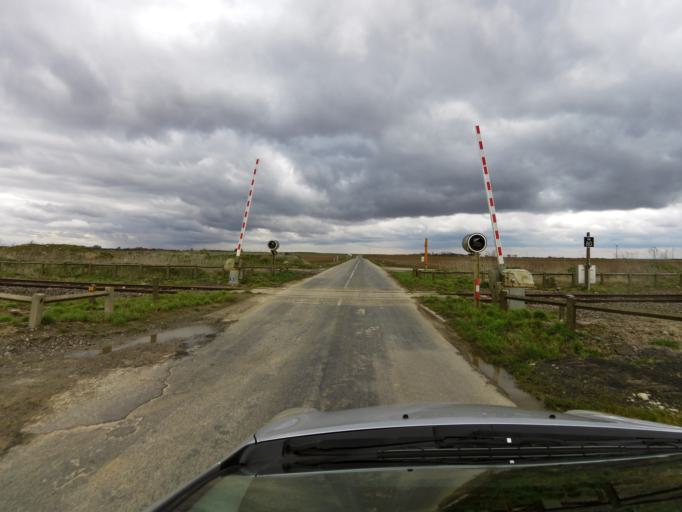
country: FR
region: Picardie
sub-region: Departement de la Somme
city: Roye
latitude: 49.7398
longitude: 2.7968
